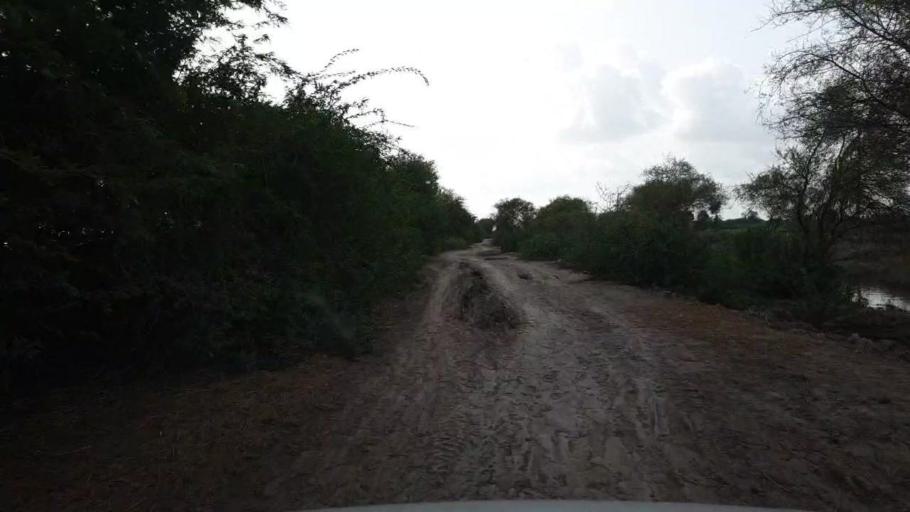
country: PK
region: Sindh
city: Kario
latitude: 24.7605
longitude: 68.6052
